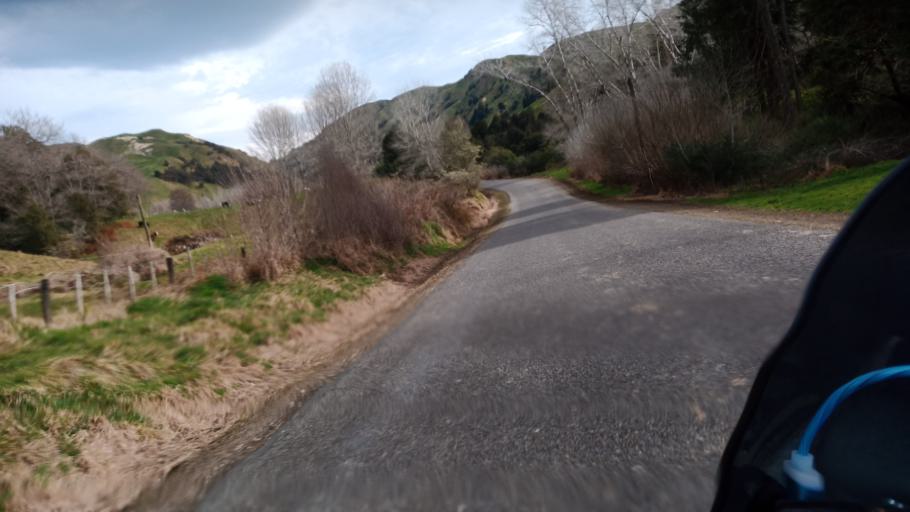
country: NZ
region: Hawke's Bay
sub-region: Wairoa District
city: Wairoa
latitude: -38.8003
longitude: 177.4564
